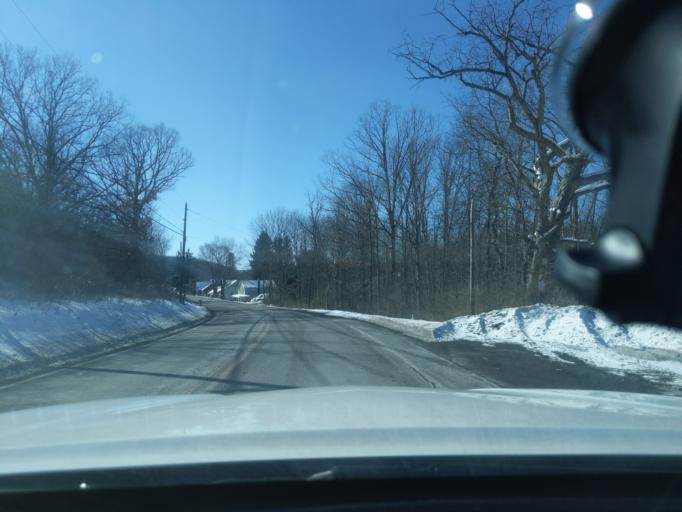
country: US
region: Maryland
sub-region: Allegany County
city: Frostburg
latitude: 39.6143
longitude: -78.9388
